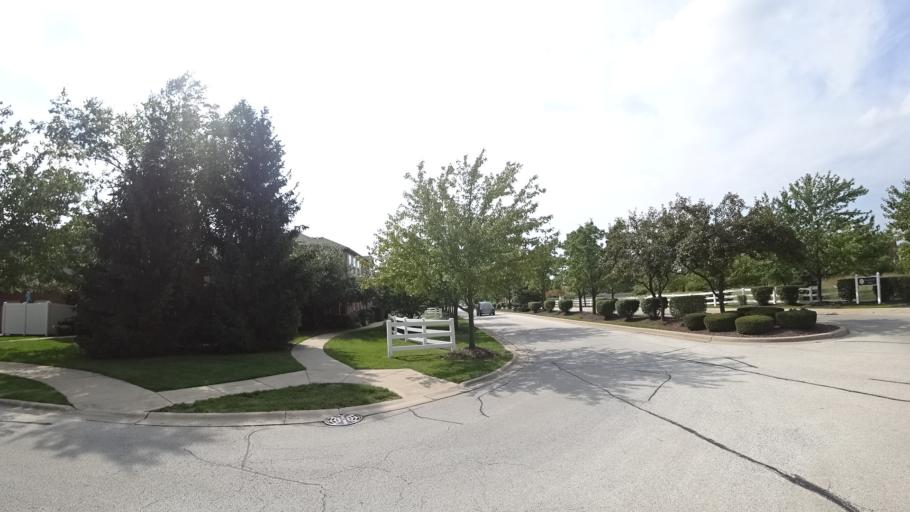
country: US
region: Illinois
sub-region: Cook County
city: Tinley Park
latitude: 41.5542
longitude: -87.7819
